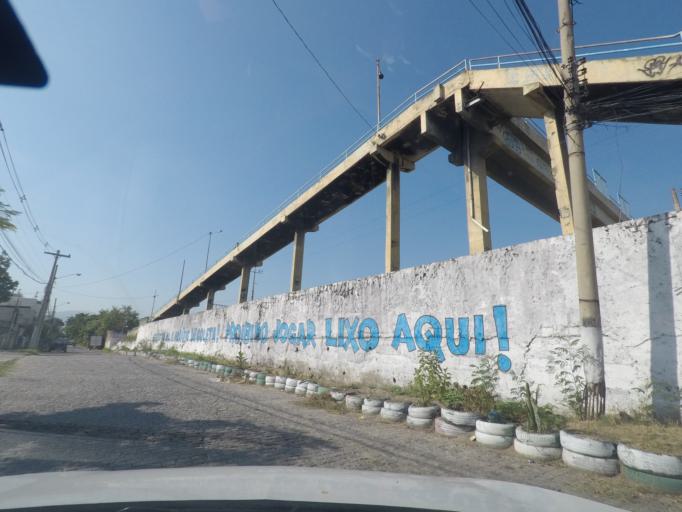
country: BR
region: Rio de Janeiro
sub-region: Rio De Janeiro
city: Rio de Janeiro
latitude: -22.8586
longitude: -43.2581
